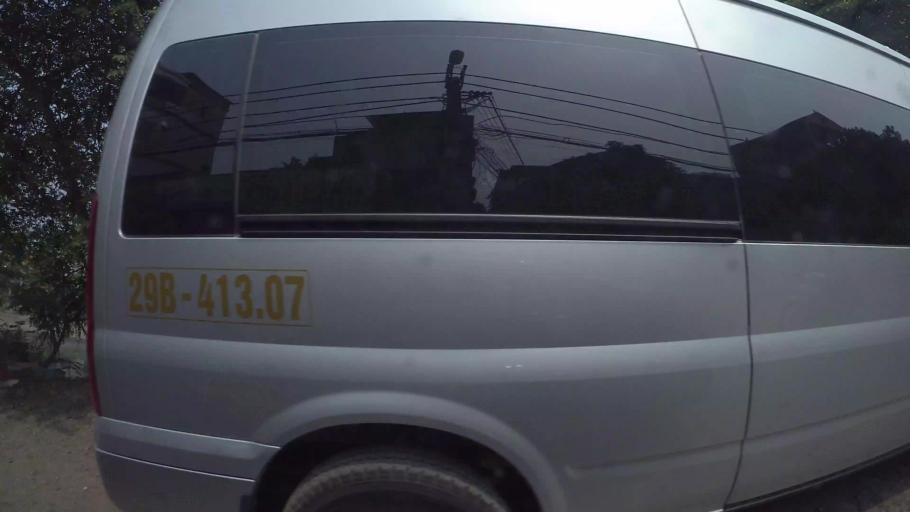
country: VN
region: Ha Noi
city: Van Dien
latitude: 20.9644
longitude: 105.8200
